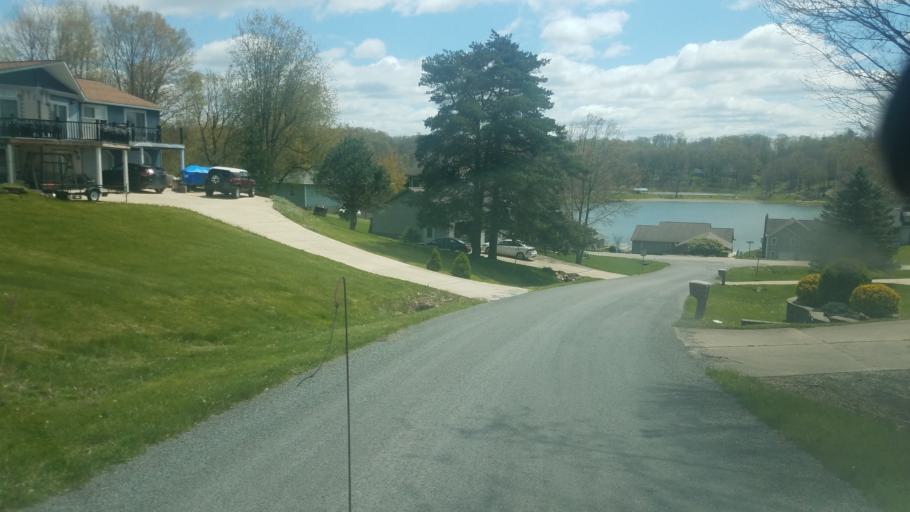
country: US
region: Ohio
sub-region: Knox County
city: Gambier
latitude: 40.4423
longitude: -82.3473
